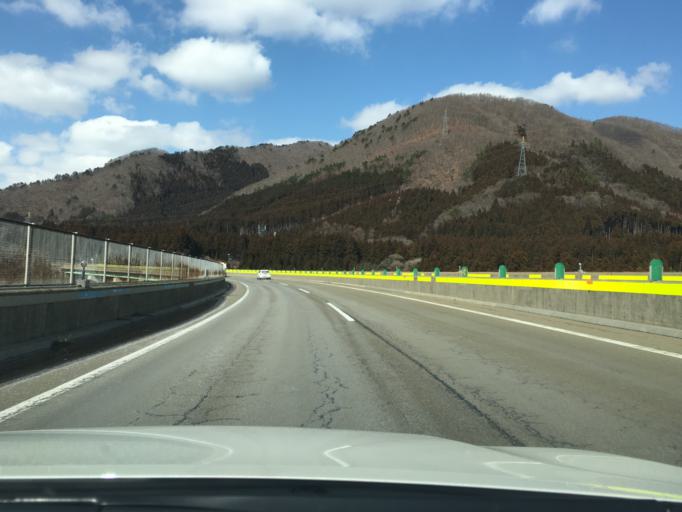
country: JP
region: Miyagi
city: Shiroishi
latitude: 38.2044
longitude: 140.5792
